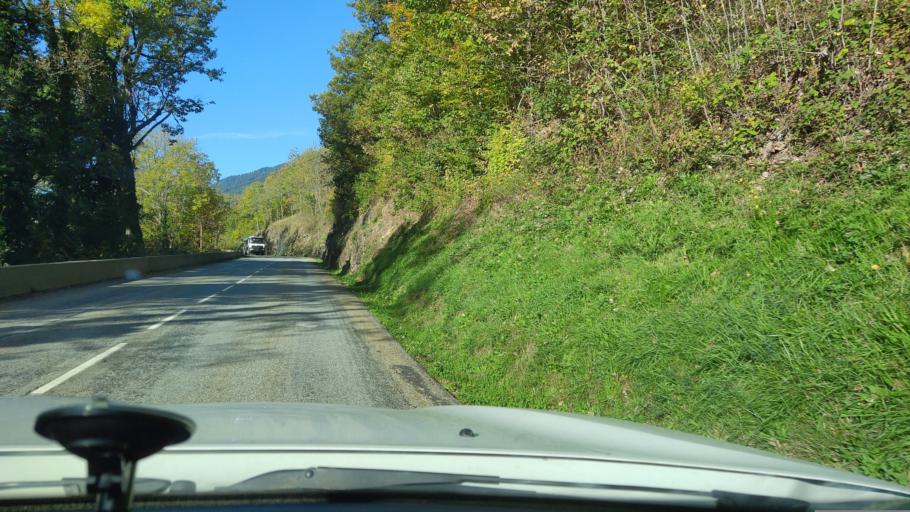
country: FR
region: Rhone-Alpes
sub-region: Departement de la Savoie
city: Beaufort
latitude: 45.7284
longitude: 6.5528
